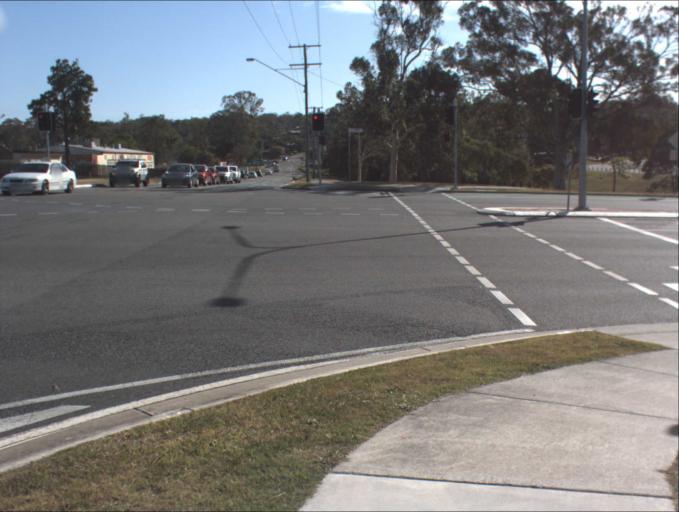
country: AU
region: Queensland
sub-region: Logan
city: Beenleigh
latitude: -27.7189
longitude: 153.1981
